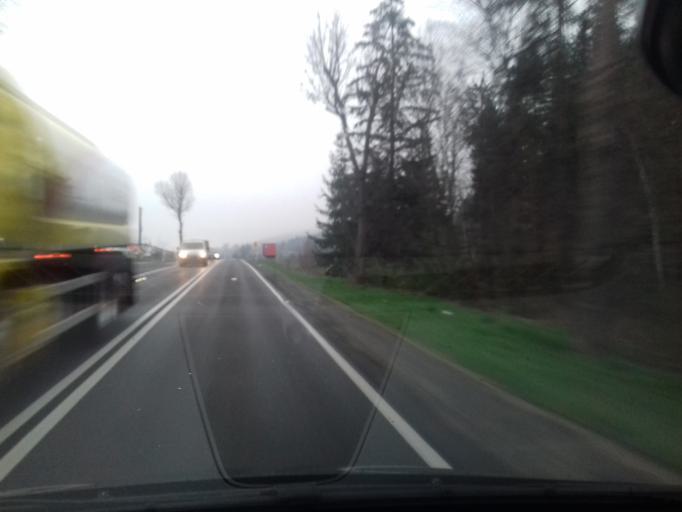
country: PL
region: Lesser Poland Voivodeship
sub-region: Powiat limanowski
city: Tymbark
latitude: 49.7214
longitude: 20.3666
